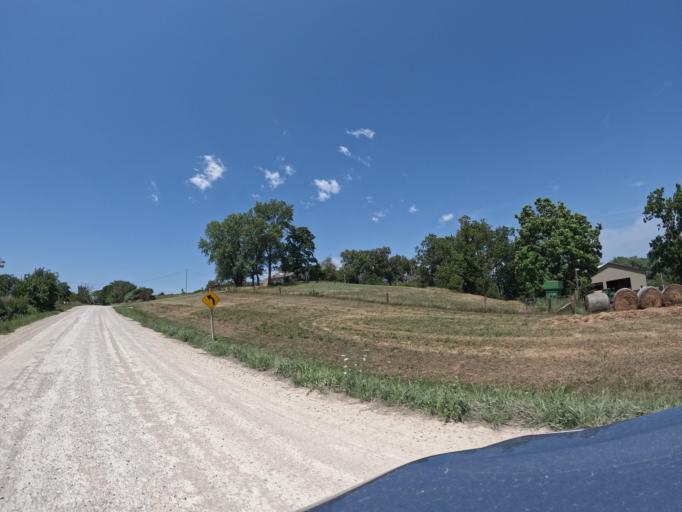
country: US
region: Iowa
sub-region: Henry County
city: Mount Pleasant
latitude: 40.9356
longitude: -91.6229
